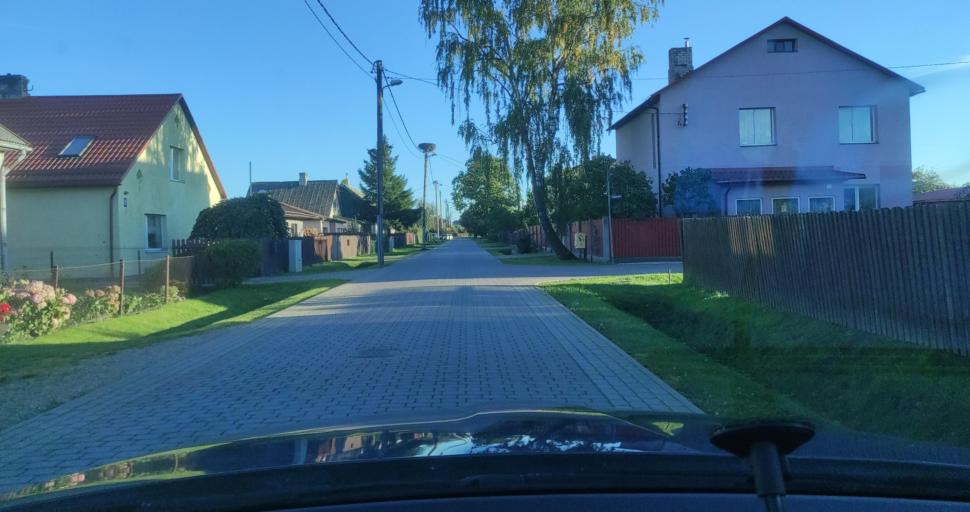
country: LV
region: Ventspils
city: Ventspils
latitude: 57.3761
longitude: 21.5762
